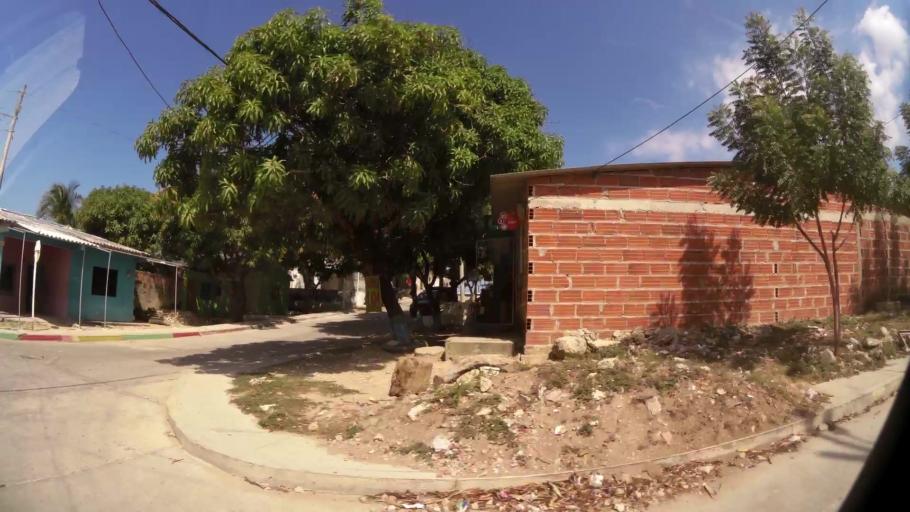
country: CO
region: Atlantico
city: Barranquilla
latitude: 10.9665
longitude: -74.8270
